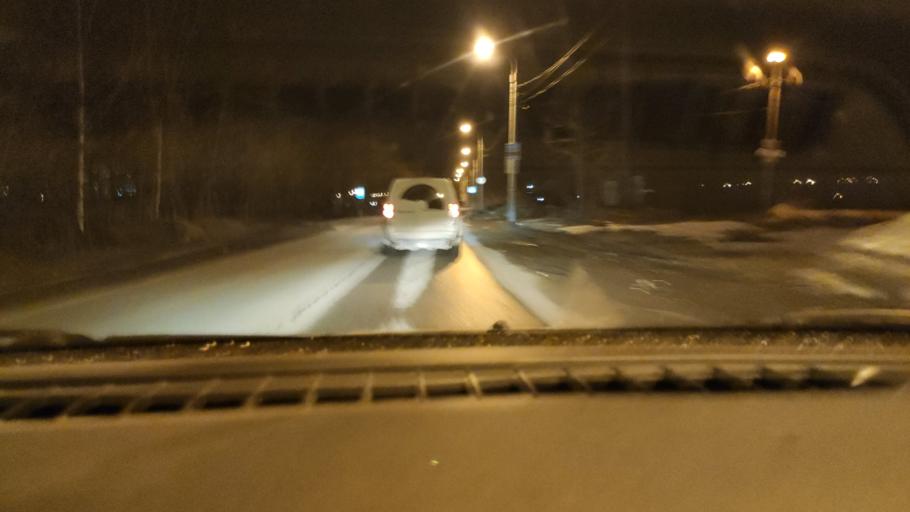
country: RU
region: Perm
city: Perm
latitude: 58.0481
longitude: 56.3387
